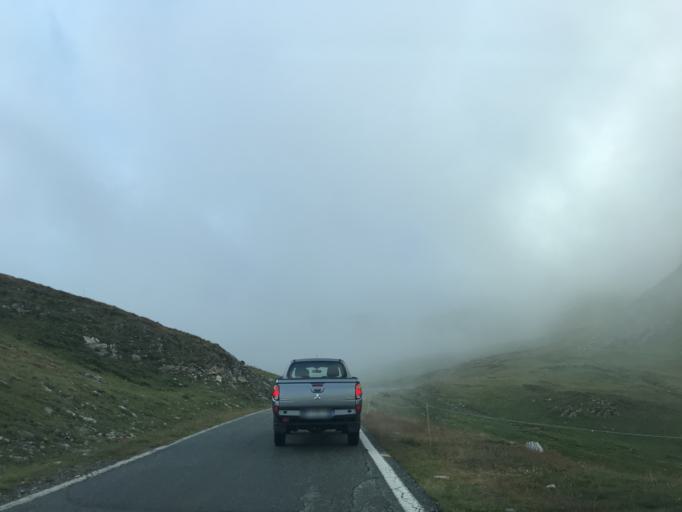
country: IT
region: Piedmont
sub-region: Provincia di Cuneo
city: Pontechianale
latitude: 44.6769
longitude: 6.9899
